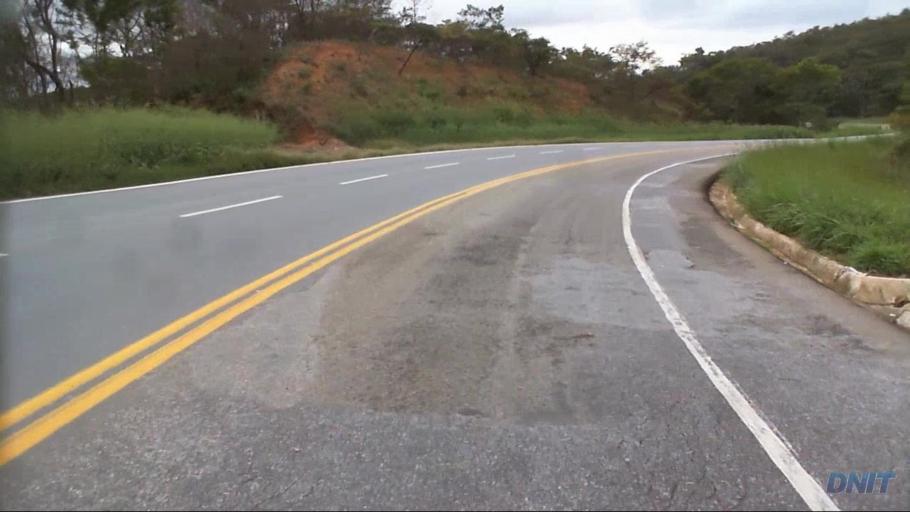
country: BR
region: Minas Gerais
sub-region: Joao Monlevade
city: Joao Monlevade
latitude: -19.8435
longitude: -43.3152
